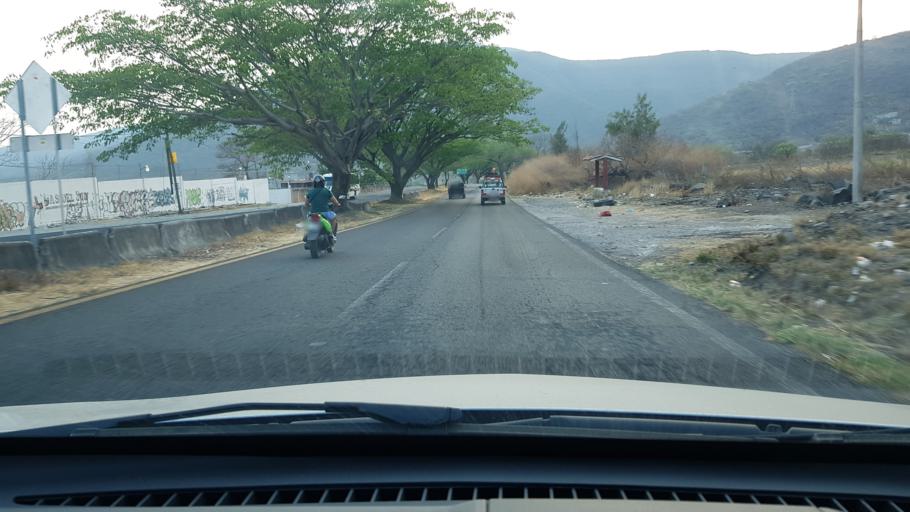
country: MX
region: Morelos
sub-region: Jiutepec
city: Independencia
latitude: 18.8599
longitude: -99.0986
